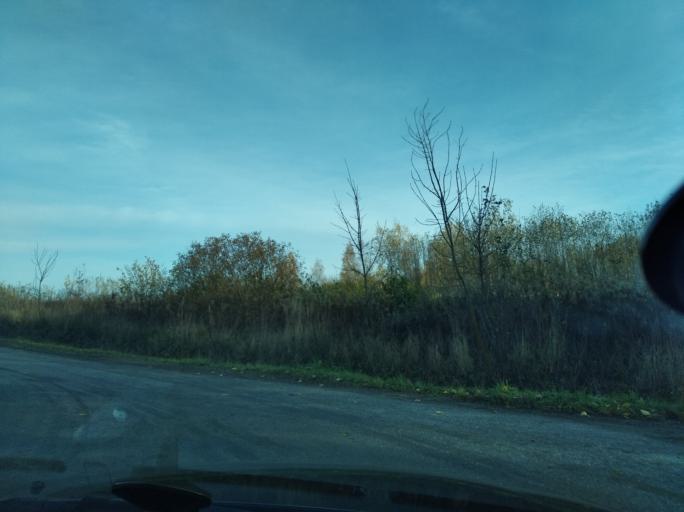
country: PL
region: Subcarpathian Voivodeship
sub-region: Powiat rzeszowski
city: Krasne
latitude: 50.0166
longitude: 22.1073
